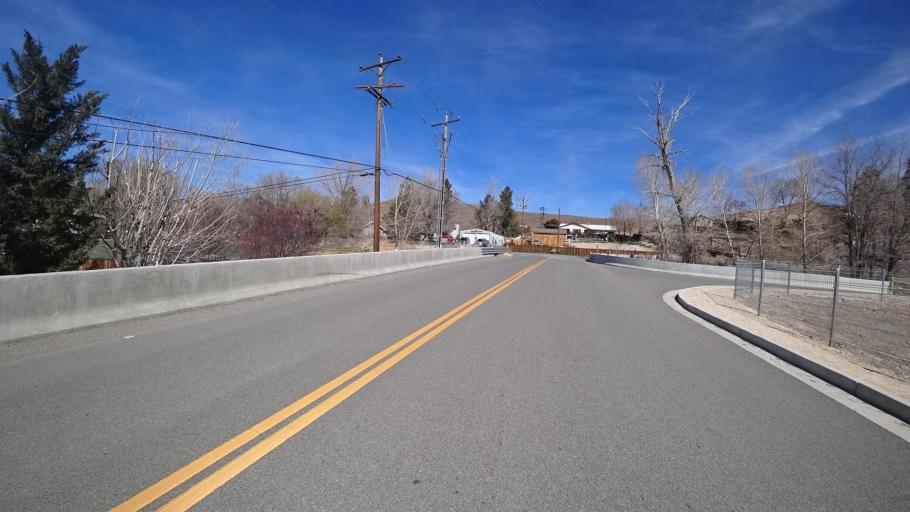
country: US
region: Nevada
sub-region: Washoe County
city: Sparks
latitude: 39.5621
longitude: -119.7523
